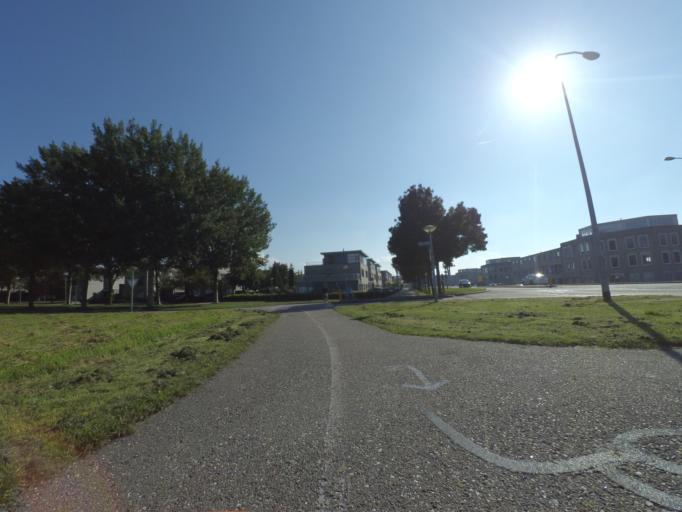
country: NL
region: Flevoland
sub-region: Gemeente Zeewolde
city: Zeewolde
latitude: 52.3351
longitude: 5.5428
